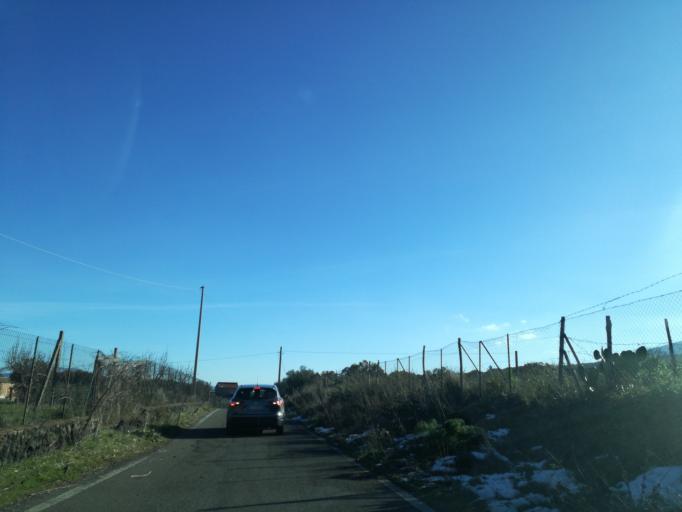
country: IT
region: Sicily
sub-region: Catania
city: Randazzo
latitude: 37.8664
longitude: 14.9806
